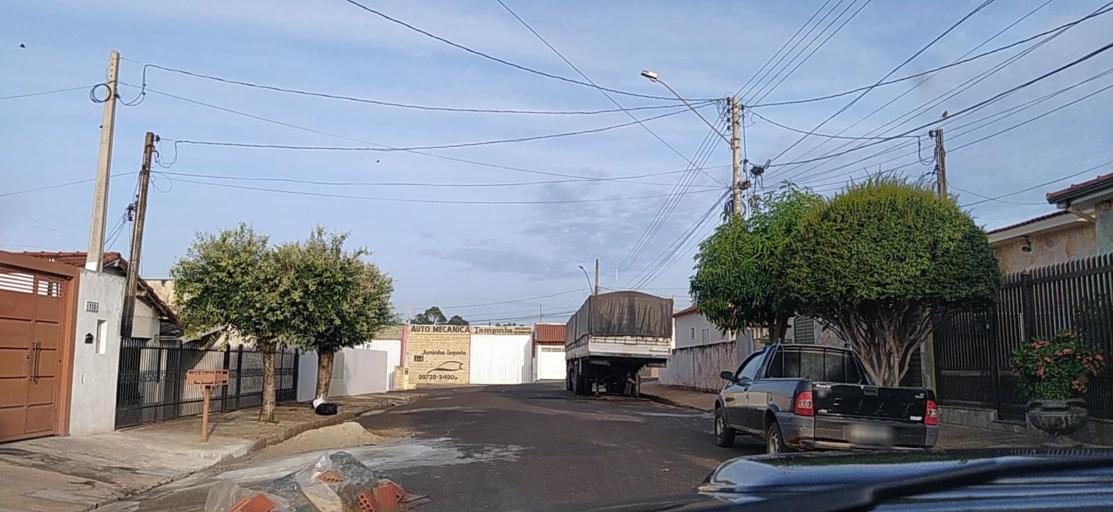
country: BR
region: Sao Paulo
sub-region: Pindorama
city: Pindorama
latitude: -21.1914
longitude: -48.9026
